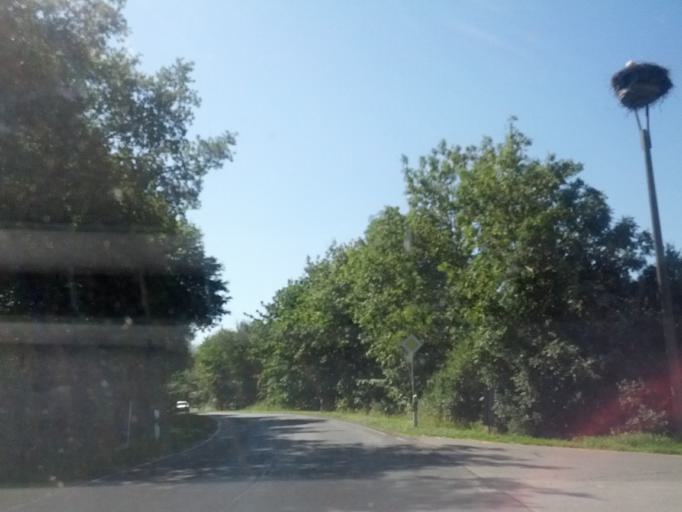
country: DE
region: Mecklenburg-Vorpommern
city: Bergen auf Ruegen
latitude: 54.4330
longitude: 13.4330
